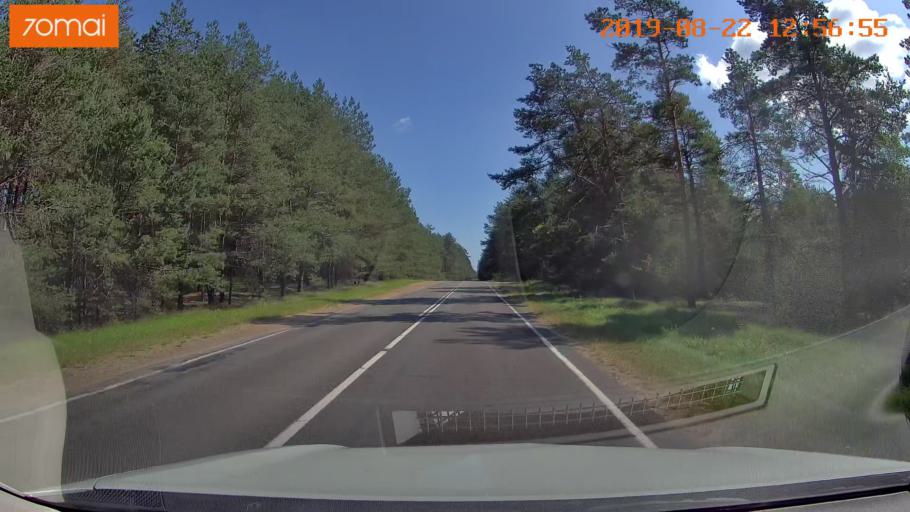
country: BY
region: Minsk
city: Prawdzinski
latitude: 53.4312
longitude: 27.7389
